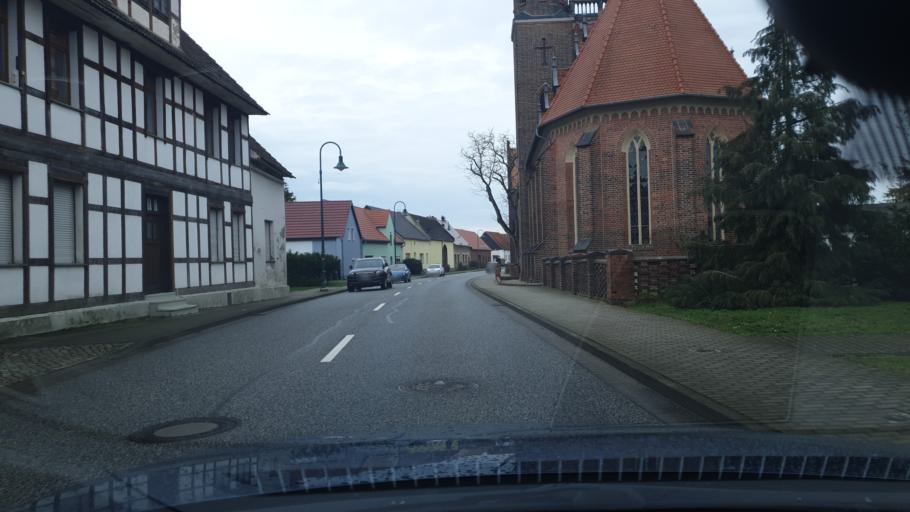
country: DE
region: Saxony-Anhalt
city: Vockerode
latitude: 51.8477
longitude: 12.3521
